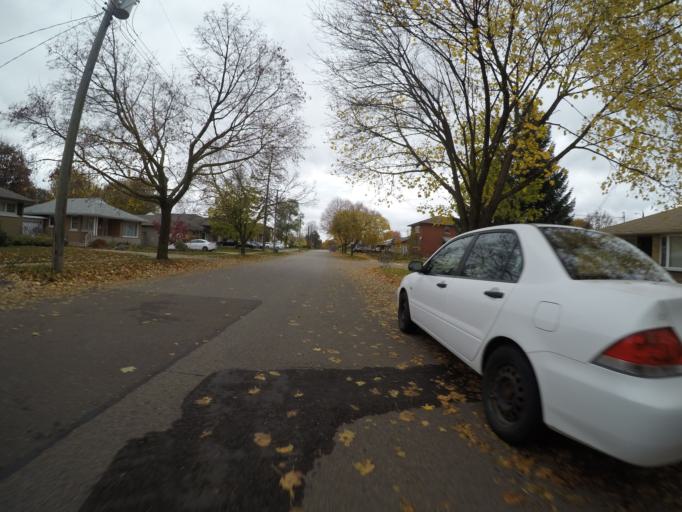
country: CA
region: Ontario
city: Kitchener
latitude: 43.4266
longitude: -80.4486
